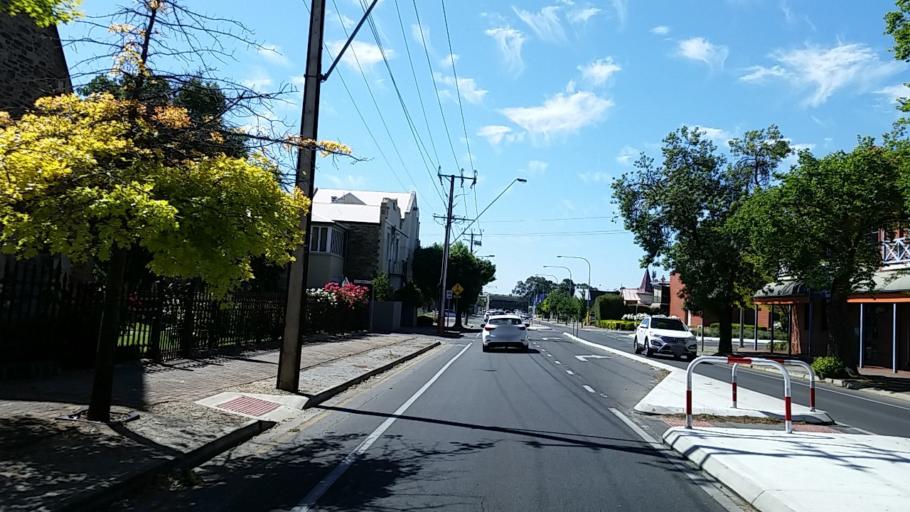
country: AU
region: South Australia
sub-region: Norwood Payneham St Peters
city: Trinity Gardens
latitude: -34.9192
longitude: 138.6230
